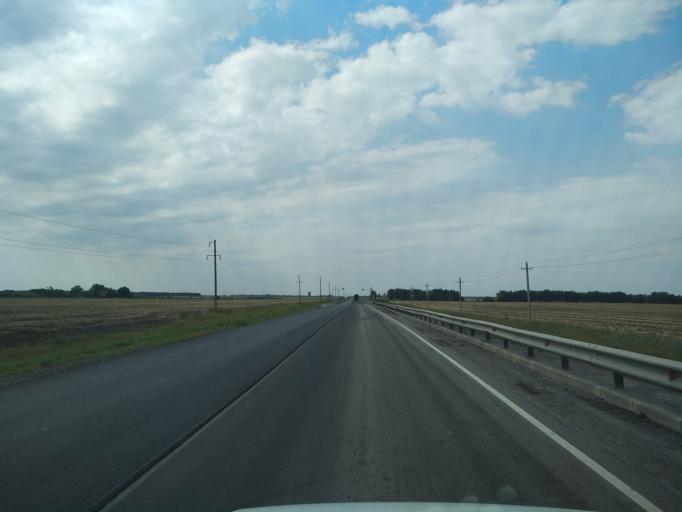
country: RU
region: Voronezj
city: Pereleshino
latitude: 51.7993
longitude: 40.1521
